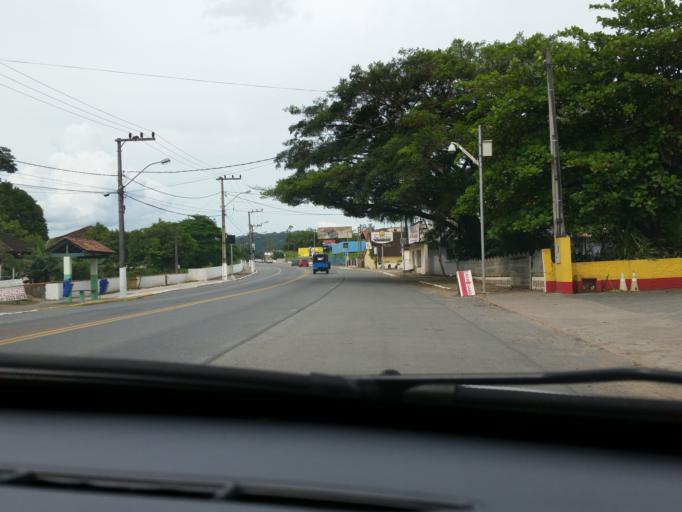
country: BR
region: Santa Catarina
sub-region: Rodeio
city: Gavea
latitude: -27.0320
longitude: -49.3848
